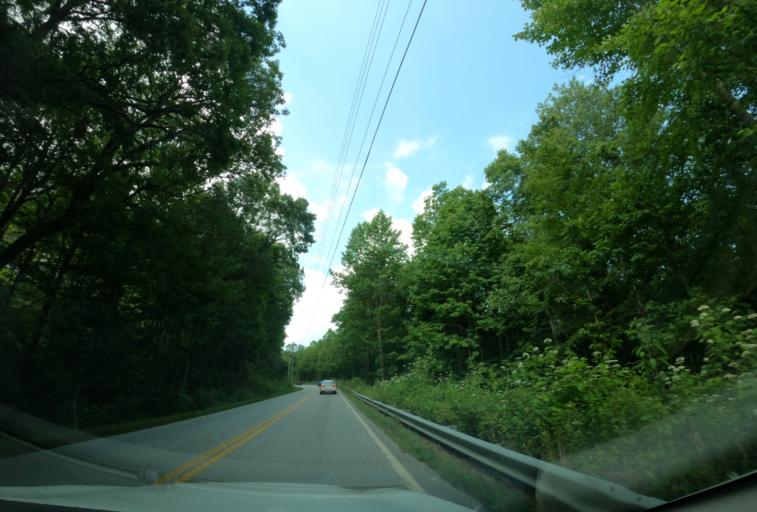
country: US
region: North Carolina
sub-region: Transylvania County
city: Brevard
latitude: 35.0958
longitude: -82.9664
